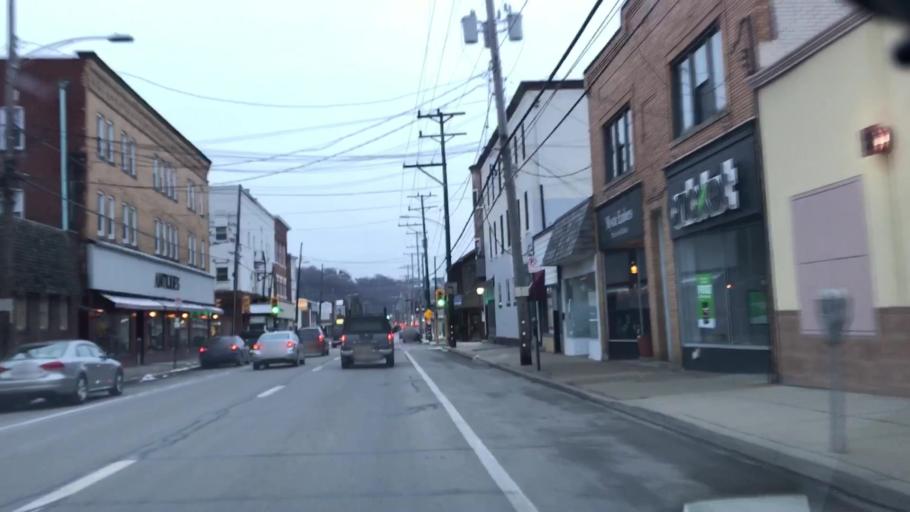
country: US
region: Pennsylvania
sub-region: Allegheny County
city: Coraopolis
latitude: 40.5181
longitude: -80.1630
